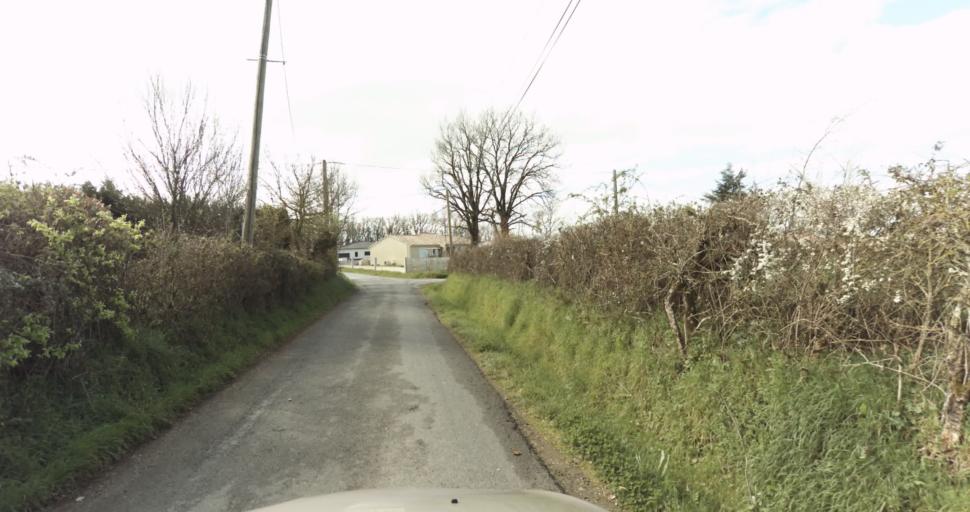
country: FR
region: Midi-Pyrenees
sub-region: Departement du Tarn
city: Frejairolles
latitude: 43.8660
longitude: 2.2057
